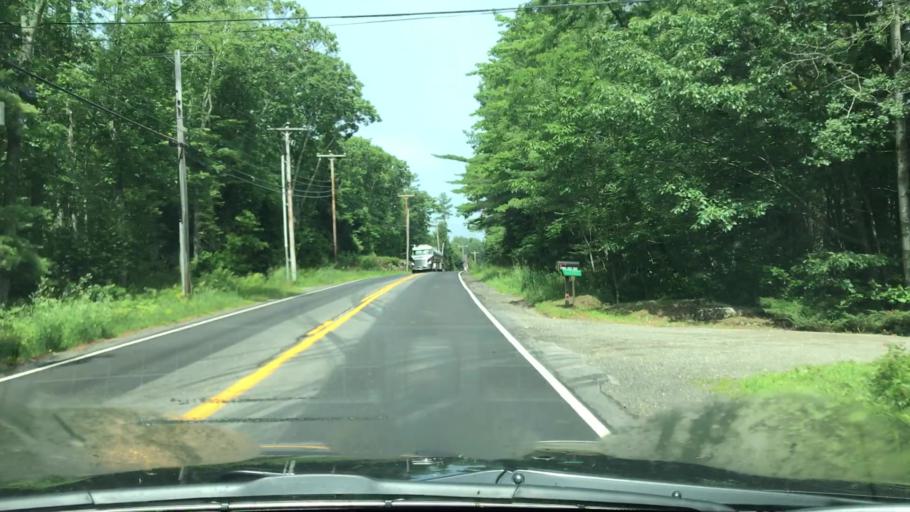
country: US
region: Maine
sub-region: Waldo County
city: Lincolnville
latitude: 44.2527
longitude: -69.0306
